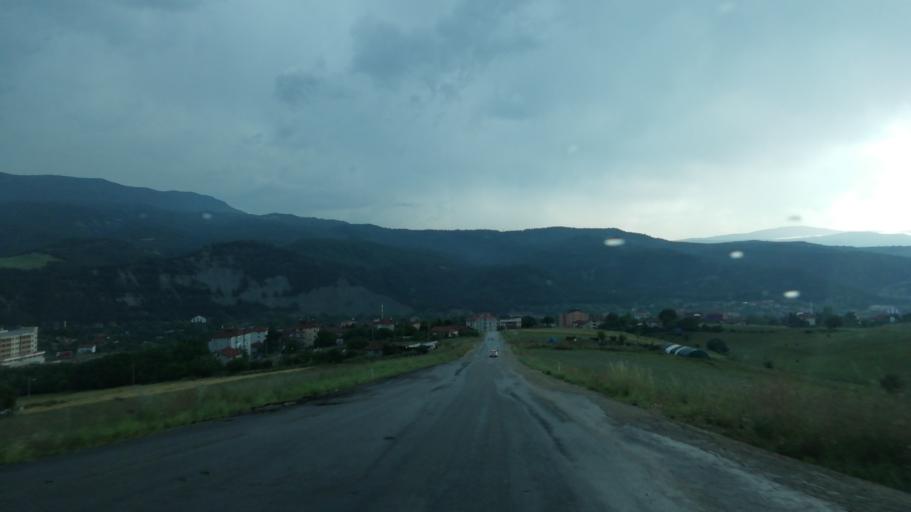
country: TR
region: Karabuk
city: Safranbolu
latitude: 41.2243
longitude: 32.6866
